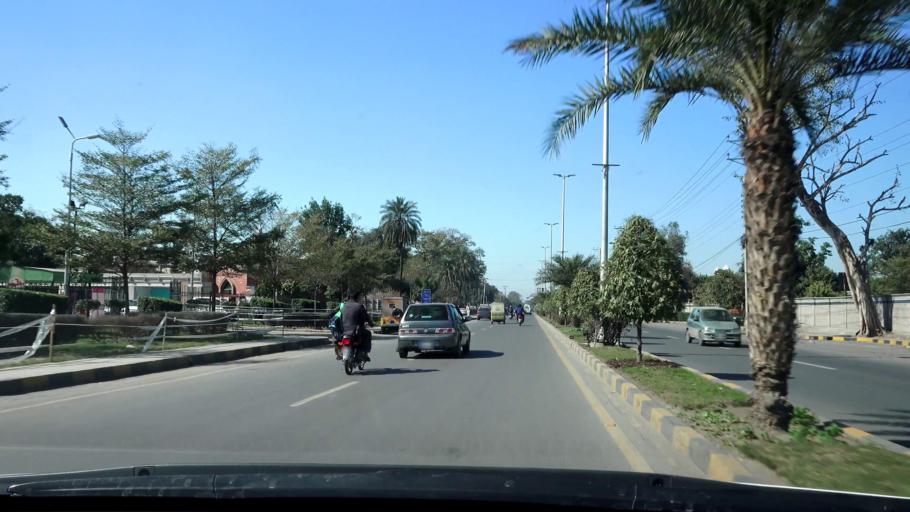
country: PK
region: Punjab
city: Faisalabad
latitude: 31.4201
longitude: 73.0868
